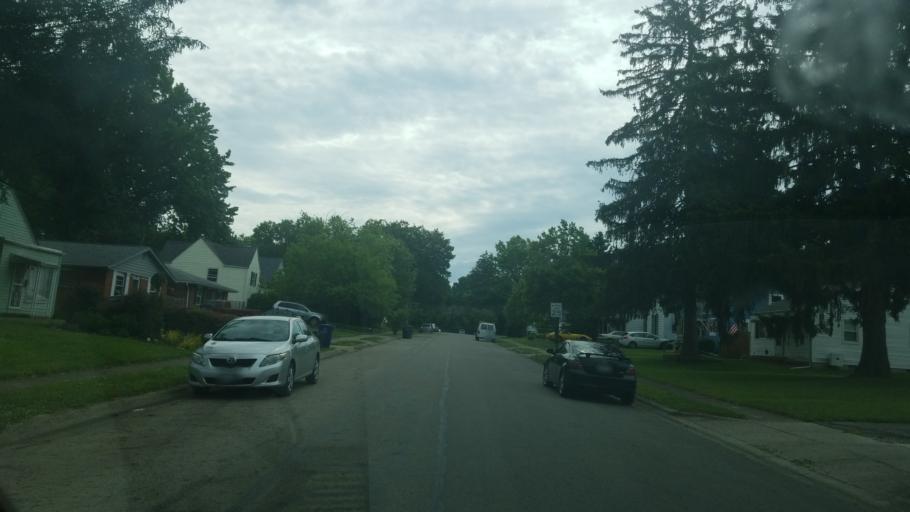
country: US
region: Ohio
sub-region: Franklin County
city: Worthington
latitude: 40.0762
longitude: -83.0113
